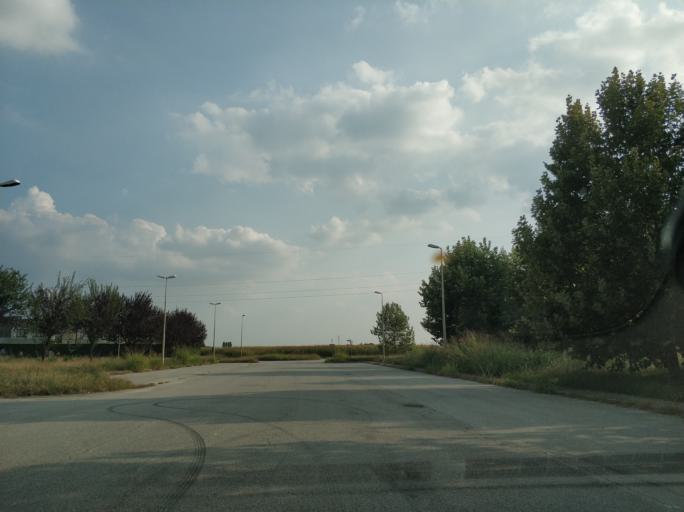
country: IT
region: Piedmont
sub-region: Provincia di Torino
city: Cirie
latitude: 45.2112
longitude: 7.6093
